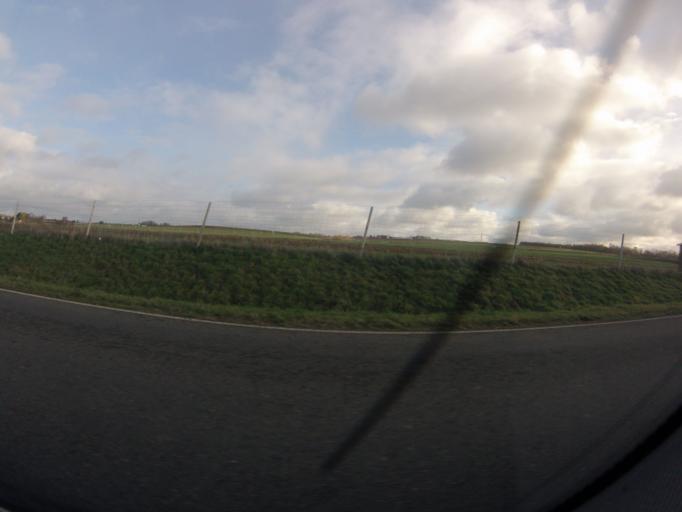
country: DE
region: Thuringia
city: Gossnitz
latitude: 50.9085
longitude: 12.4411
